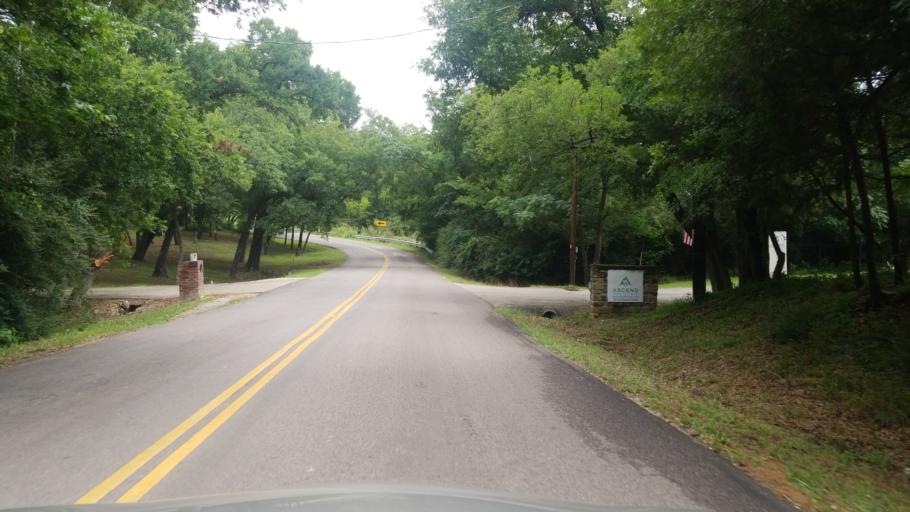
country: US
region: Texas
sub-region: Dallas County
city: Duncanville
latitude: 32.6854
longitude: -96.9341
